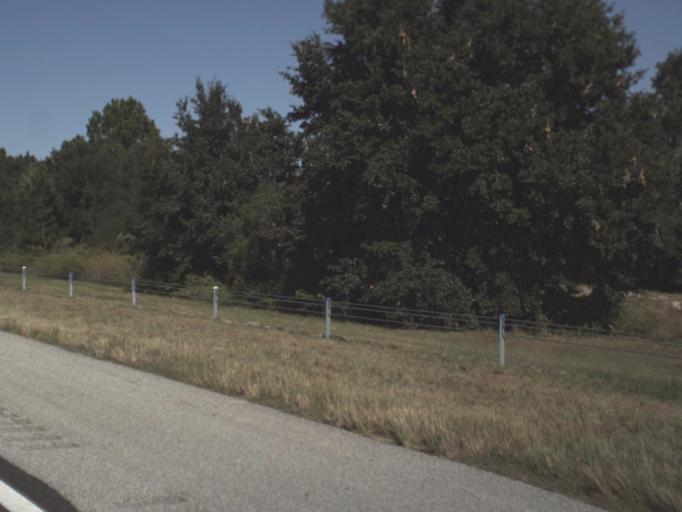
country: US
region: Florida
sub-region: Lake County
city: Hawthorne
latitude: 28.6871
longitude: -81.8667
